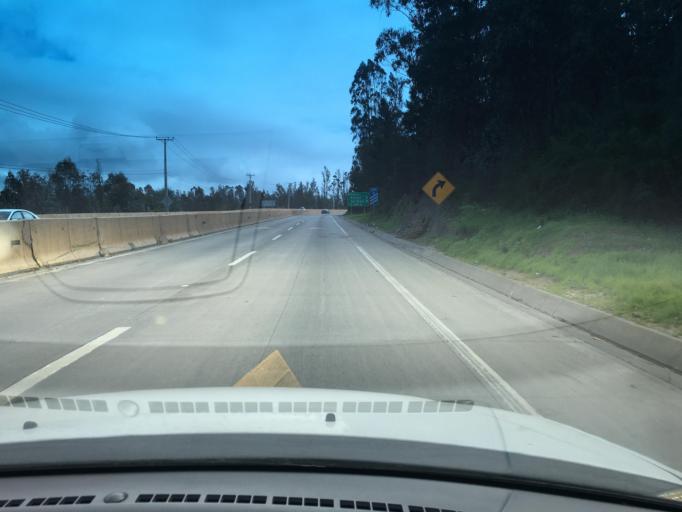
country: CL
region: Valparaiso
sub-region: Provincia de Valparaiso
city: Valparaiso
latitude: -33.0982
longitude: -71.5771
